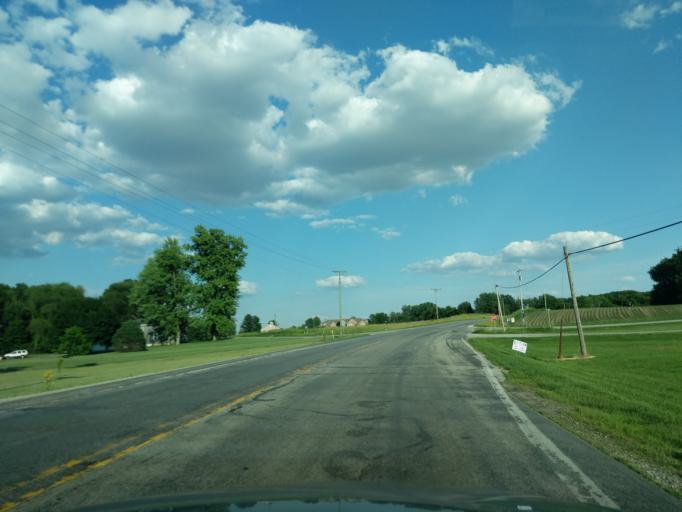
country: US
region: Indiana
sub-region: Whitley County
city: Columbia City
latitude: 41.1185
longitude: -85.4740
